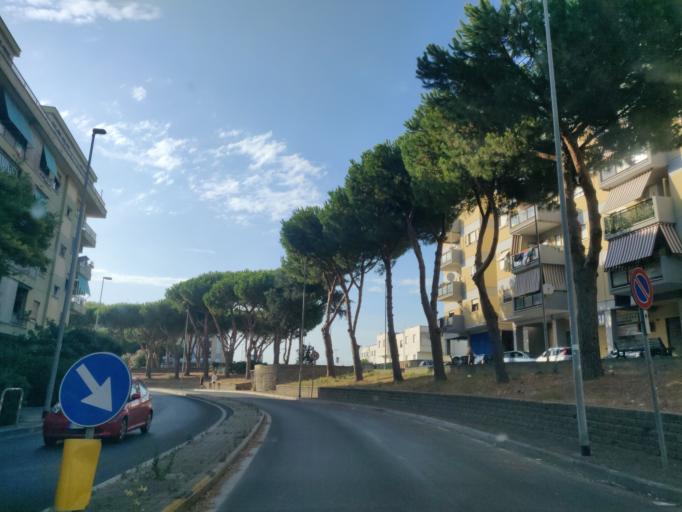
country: IT
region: Latium
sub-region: Citta metropolitana di Roma Capitale
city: Civitavecchia
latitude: 42.0817
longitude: 11.8137
